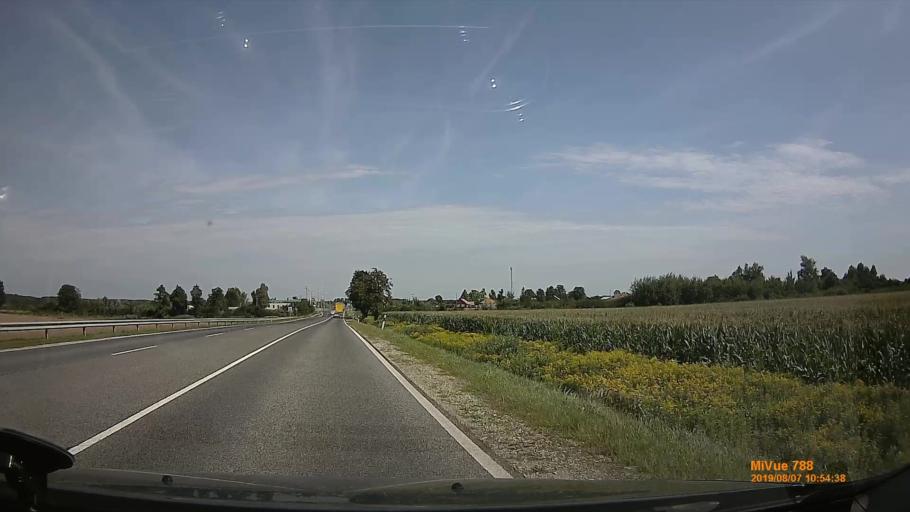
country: SI
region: Lendava-Lendva
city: Lendava
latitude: 46.6123
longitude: 16.4640
